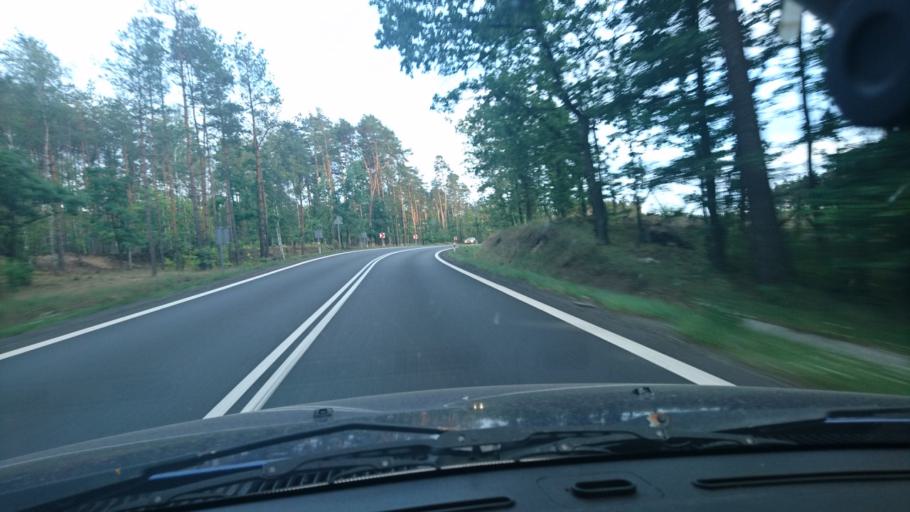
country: PL
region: Silesian Voivodeship
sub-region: Powiat tarnogorski
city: Tworog
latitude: 50.5847
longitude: 18.7065
